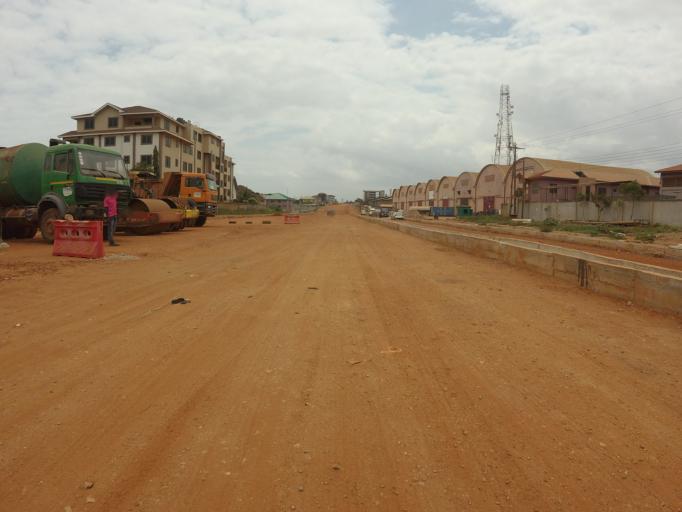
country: GH
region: Greater Accra
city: Medina Estates
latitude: 5.6274
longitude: -0.1470
